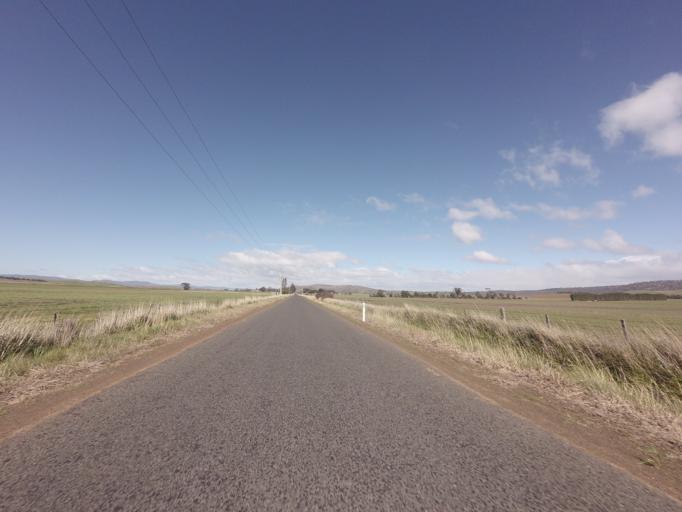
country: AU
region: Tasmania
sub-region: Northern Midlands
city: Evandale
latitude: -41.9959
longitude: 147.4543
